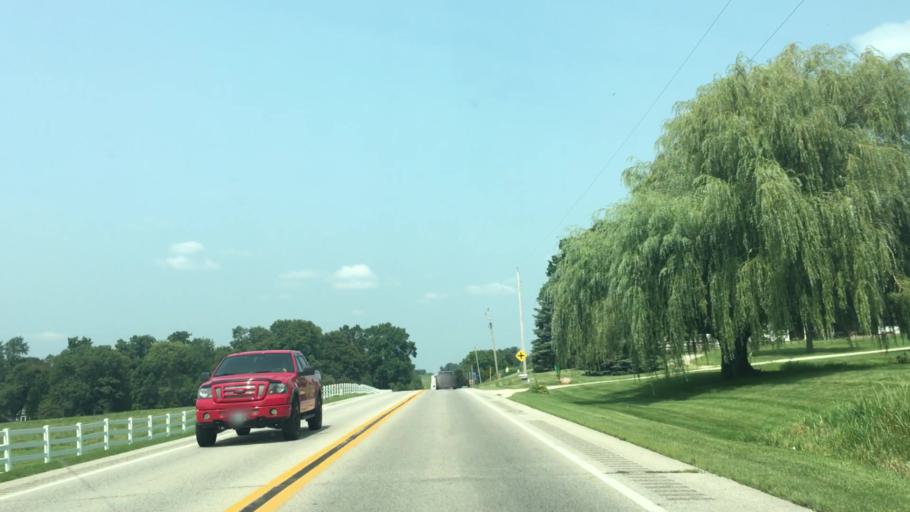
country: US
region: Iowa
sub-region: Buchanan County
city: Independence
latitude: 42.4947
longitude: -91.8895
